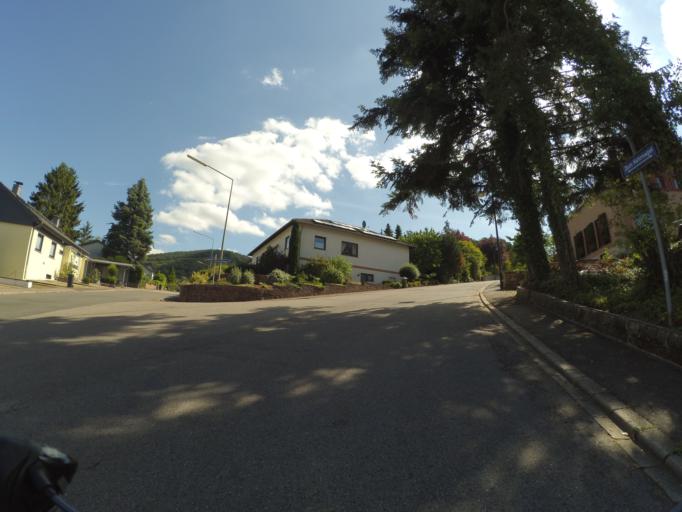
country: DE
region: Rheinland-Pfalz
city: Kasel
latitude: 49.7616
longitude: 6.7357
